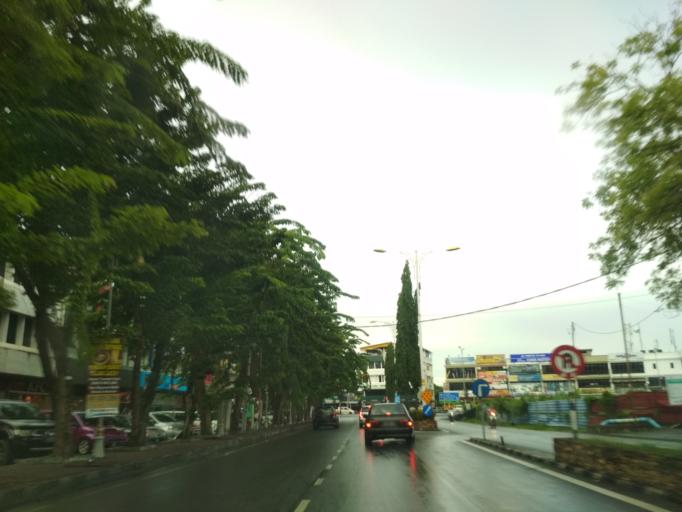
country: MY
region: Perlis
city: Kangar
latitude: 6.4357
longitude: 100.1938
